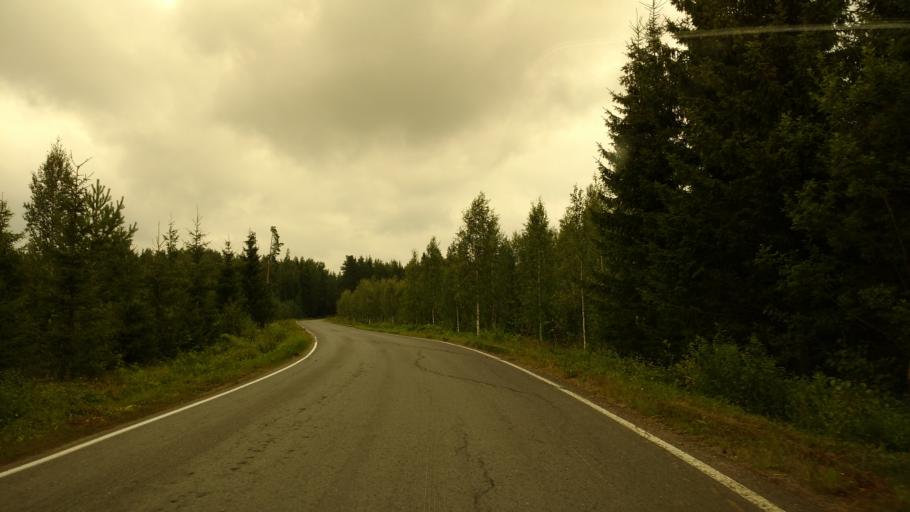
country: FI
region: Haeme
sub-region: Forssa
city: Ypaejae
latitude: 60.7456
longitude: 23.2023
